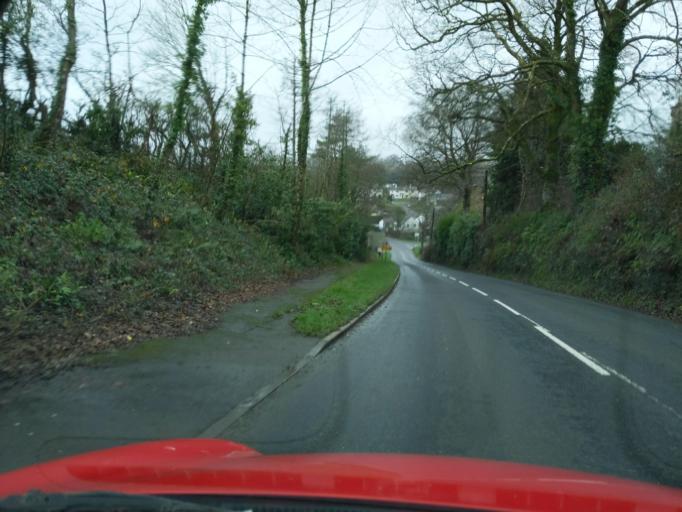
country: GB
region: England
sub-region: Devon
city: Holsworthy
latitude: 50.8055
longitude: -4.3478
